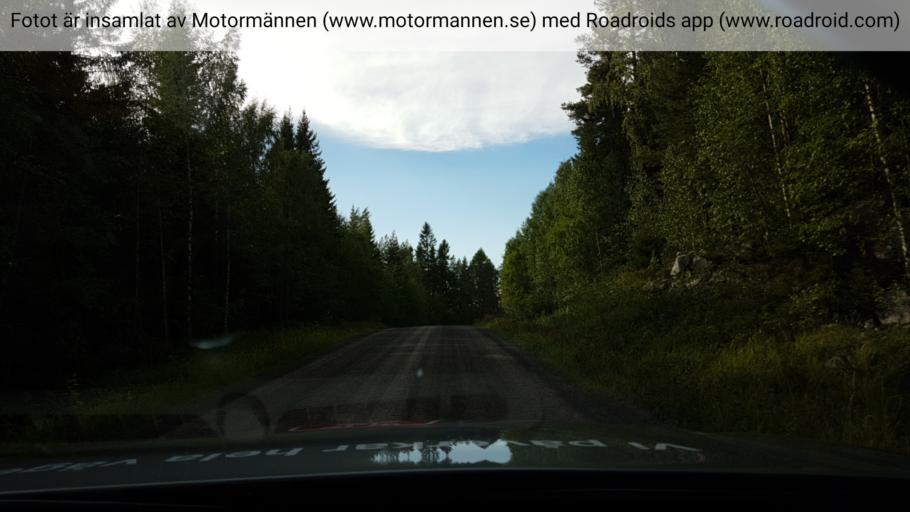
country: SE
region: Jaemtland
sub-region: Braecke Kommun
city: Braecke
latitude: 63.2113
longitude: 15.3774
